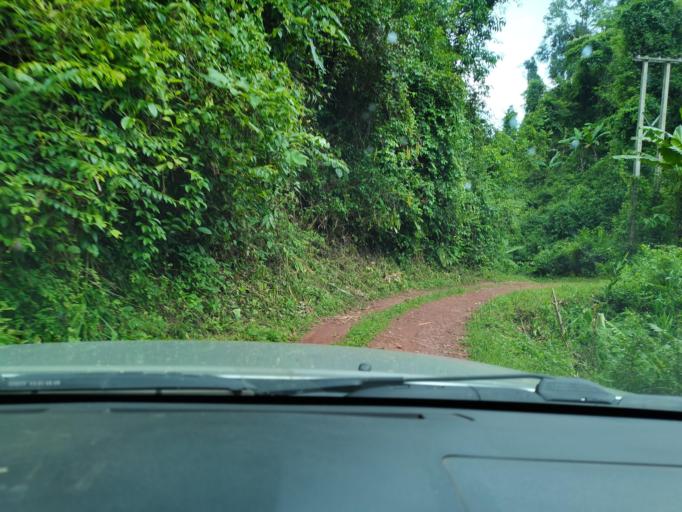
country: LA
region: Loungnamtha
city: Muang Nale
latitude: 20.5166
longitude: 101.0713
